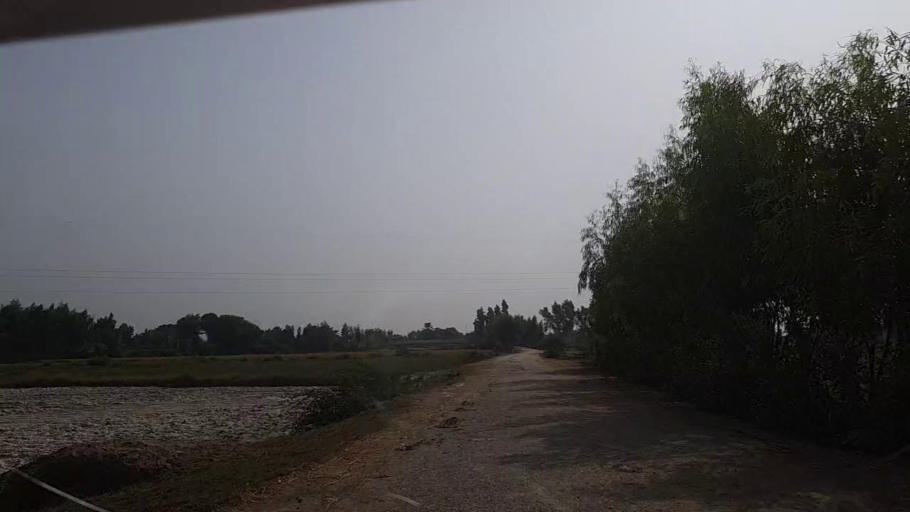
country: PK
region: Sindh
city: Madeji
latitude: 27.7358
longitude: 68.4358
